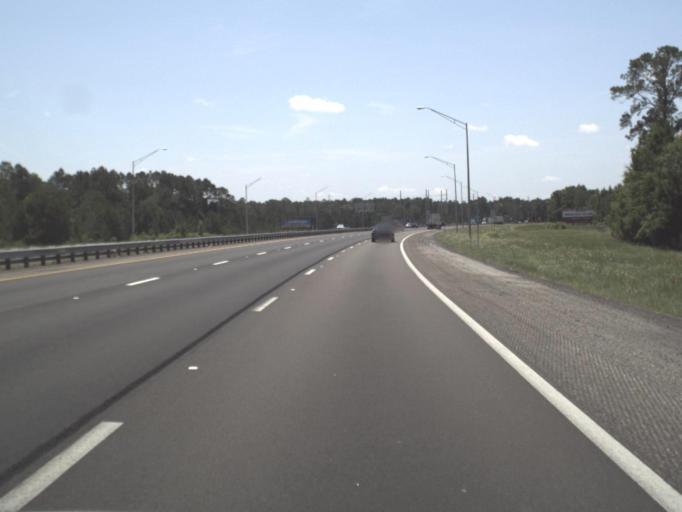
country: US
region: Florida
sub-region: Nassau County
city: Yulee
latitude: 30.5091
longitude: -81.6345
